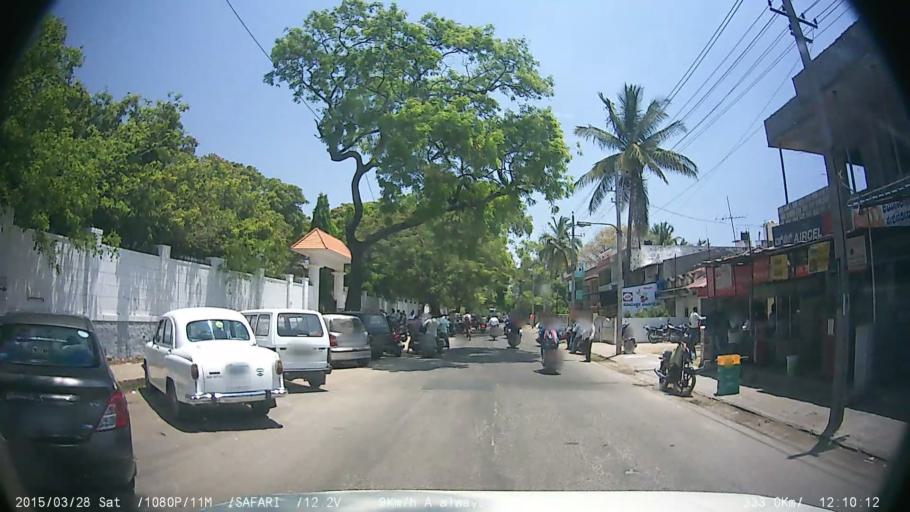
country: IN
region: Karnataka
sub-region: Mysore
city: Mysore
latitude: 12.3061
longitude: 76.6455
